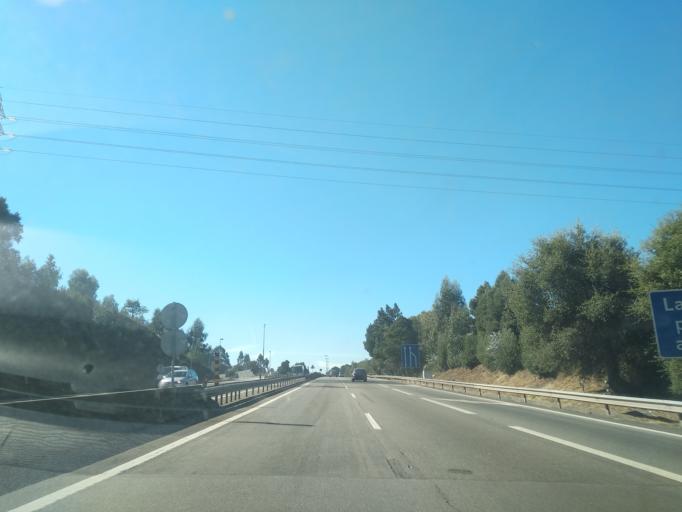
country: PT
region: Porto
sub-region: Vila Nova de Gaia
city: Perozinho
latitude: 41.0780
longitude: -8.5772
